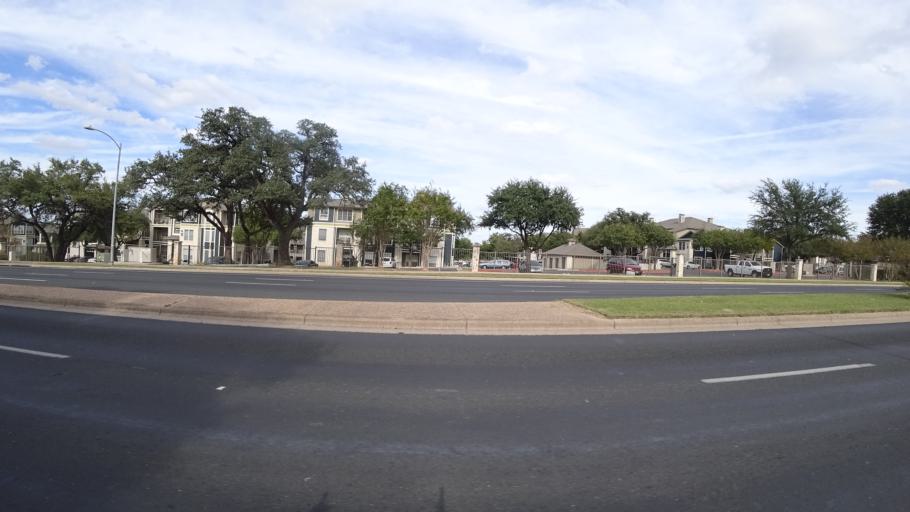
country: US
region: Texas
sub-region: Travis County
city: Onion Creek
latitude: 30.2033
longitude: -97.7722
